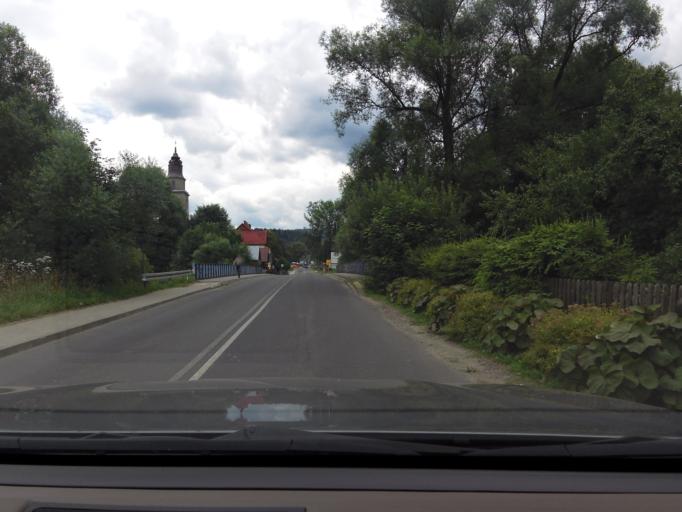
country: PL
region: Silesian Voivodeship
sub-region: Powiat zywiecki
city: Ujsoly
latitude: 49.4802
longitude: 19.1410
